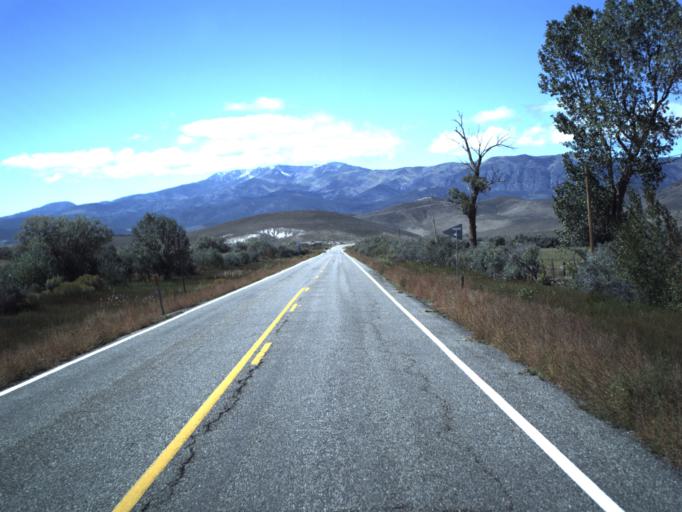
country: US
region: Utah
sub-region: Piute County
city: Junction
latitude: 38.2084
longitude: -112.2008
